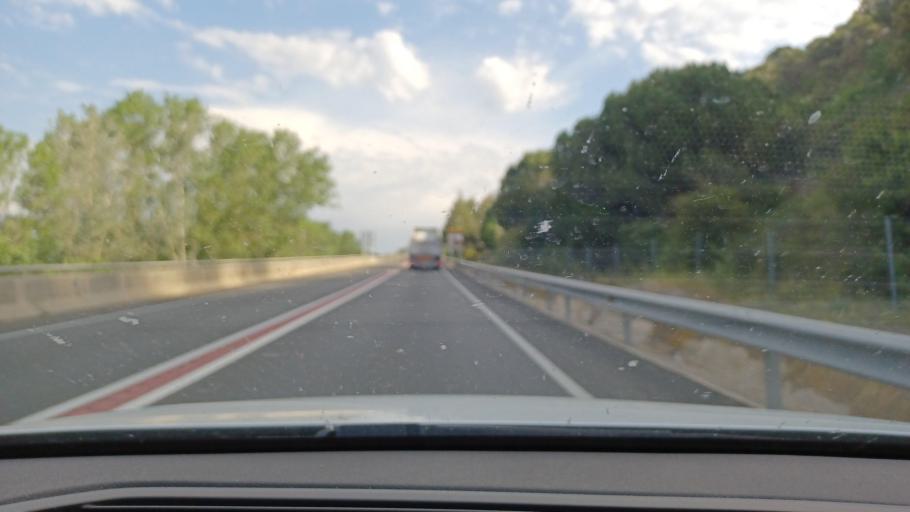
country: ES
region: Catalonia
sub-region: Provincia de Barcelona
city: Capellades
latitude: 41.5333
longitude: 1.6915
